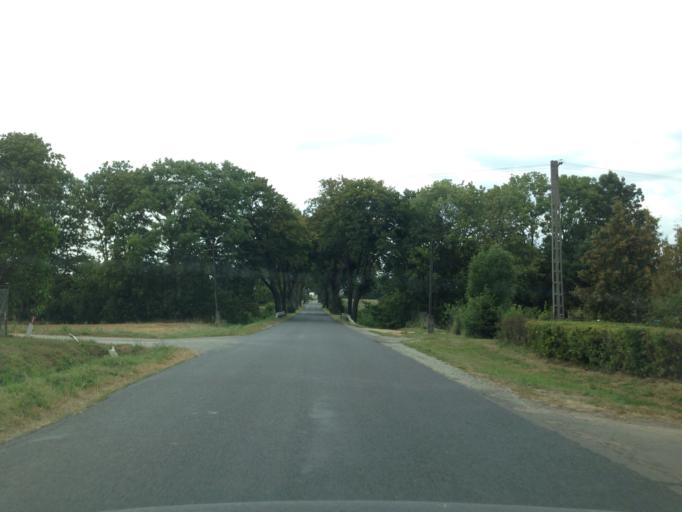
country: PL
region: Kujawsko-Pomorskie
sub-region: Powiat wabrzeski
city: Pluznica
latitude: 53.2041
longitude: 18.7954
